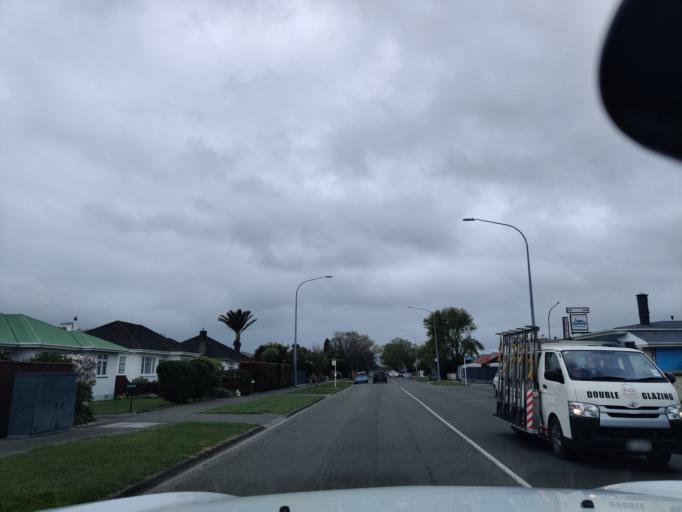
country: NZ
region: Manawatu-Wanganui
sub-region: Palmerston North City
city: Palmerston North
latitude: -40.3336
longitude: 175.6326
